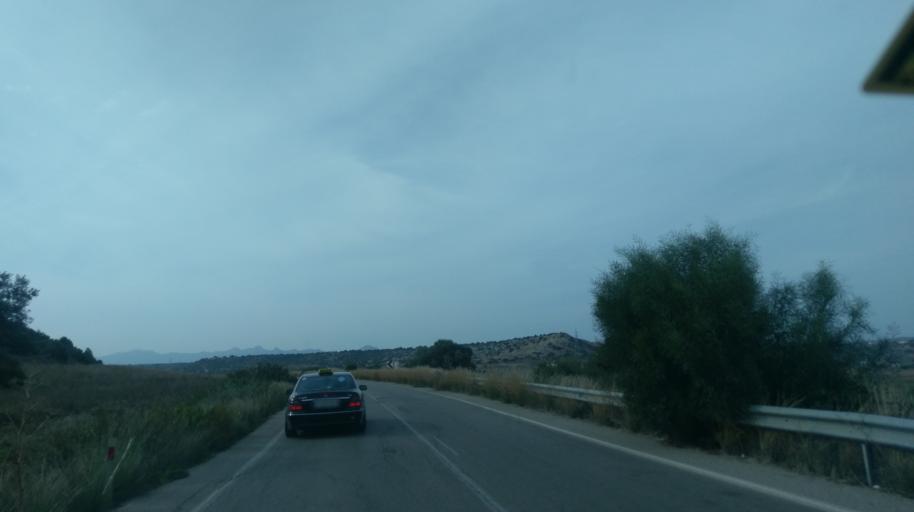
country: CY
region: Ammochostos
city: Leonarisso
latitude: 35.4022
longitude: 34.0838
